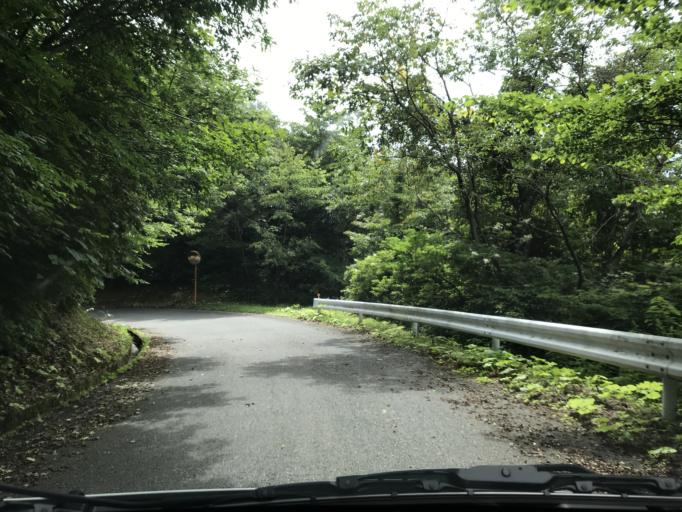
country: JP
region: Iwate
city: Ofunato
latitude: 38.9808
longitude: 141.4413
